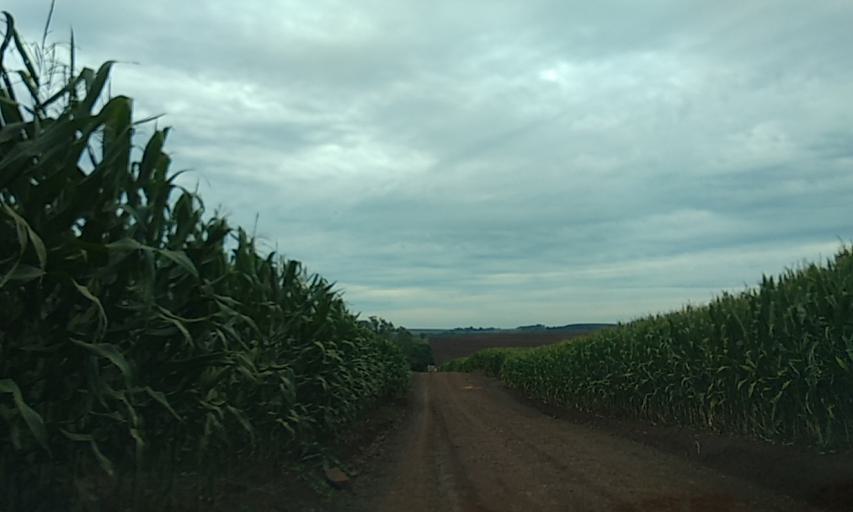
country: BR
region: Parana
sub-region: Marechal Candido Rondon
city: Marechal Candido Rondon
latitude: -24.5332
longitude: -54.0891
